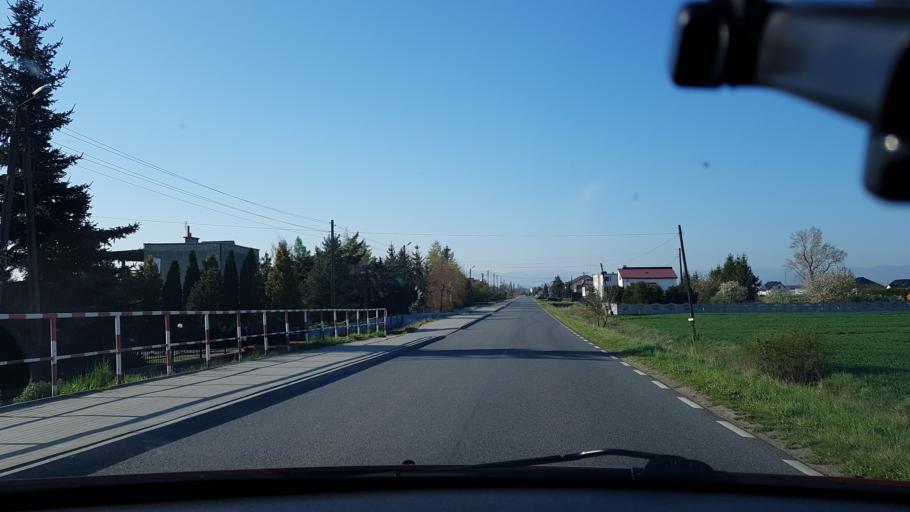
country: PL
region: Opole Voivodeship
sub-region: Powiat nyski
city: Otmuchow
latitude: 50.4519
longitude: 17.1660
